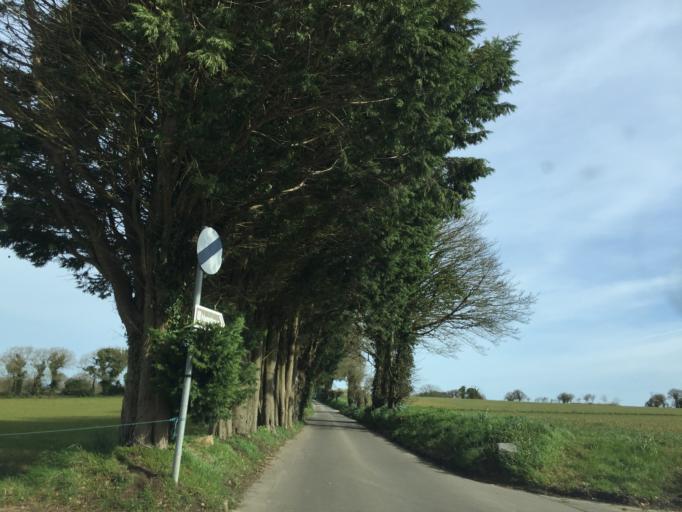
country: JE
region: St Helier
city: Saint Helier
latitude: 49.2193
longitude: -2.1399
